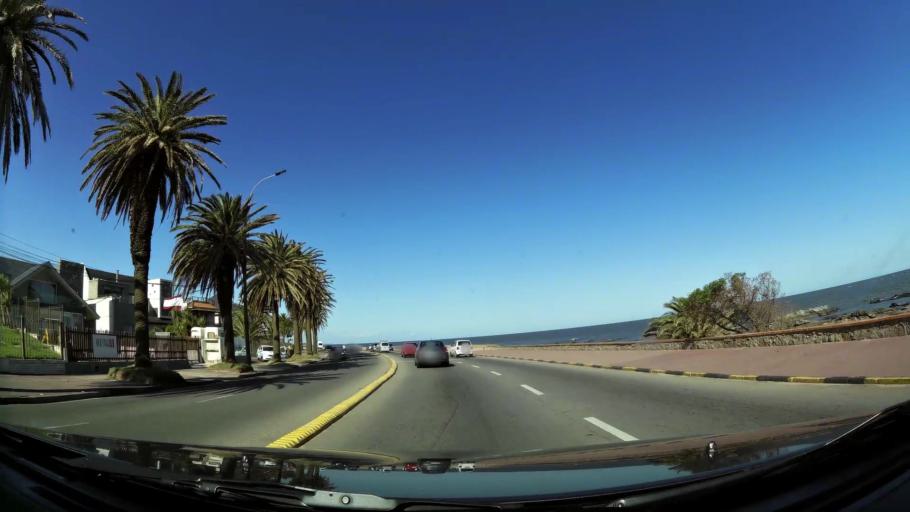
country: UY
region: Canelones
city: Paso de Carrasco
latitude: -34.8993
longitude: -56.0651
